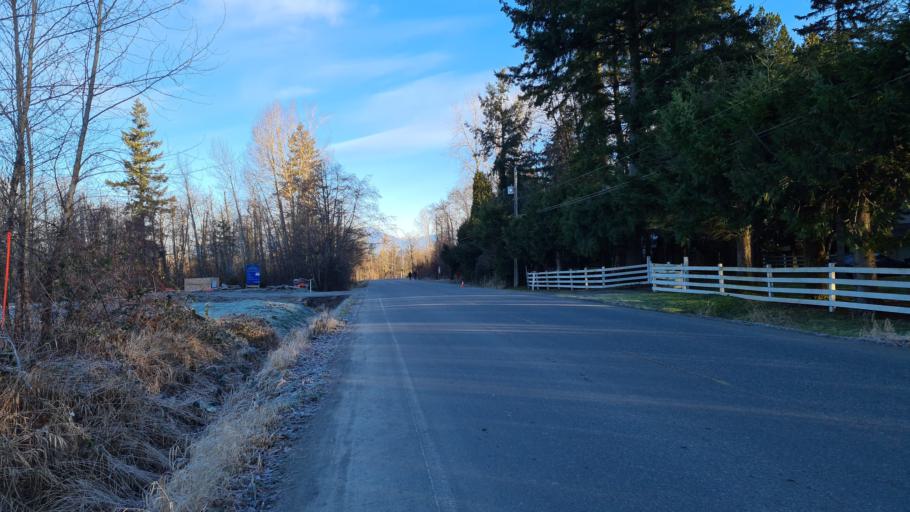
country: CA
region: British Columbia
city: Langley
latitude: 49.1385
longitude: -122.6723
